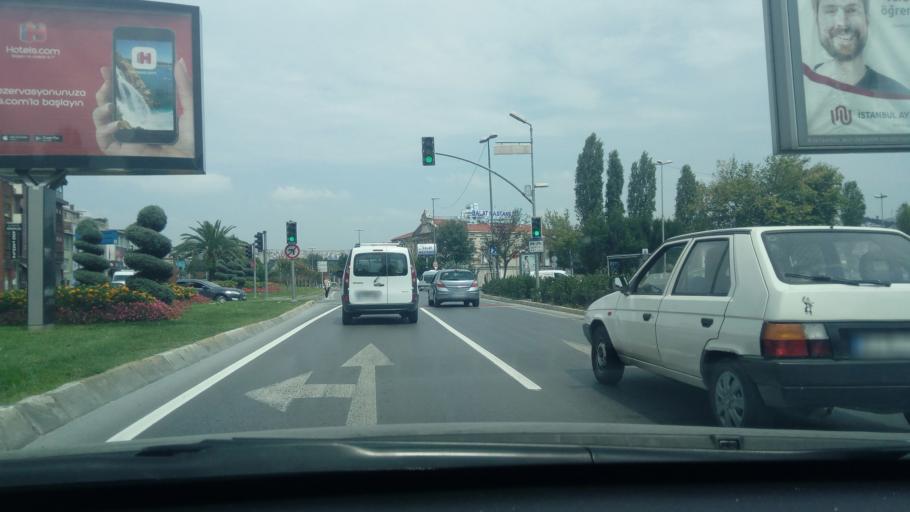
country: TR
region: Istanbul
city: Istanbul
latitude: 41.0370
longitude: 28.9453
